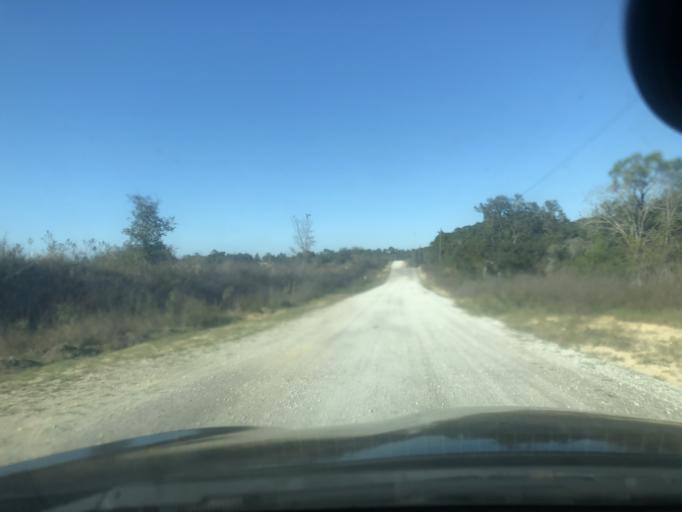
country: US
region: Florida
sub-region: Citrus County
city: Lecanto
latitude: 28.8213
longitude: -82.5179
